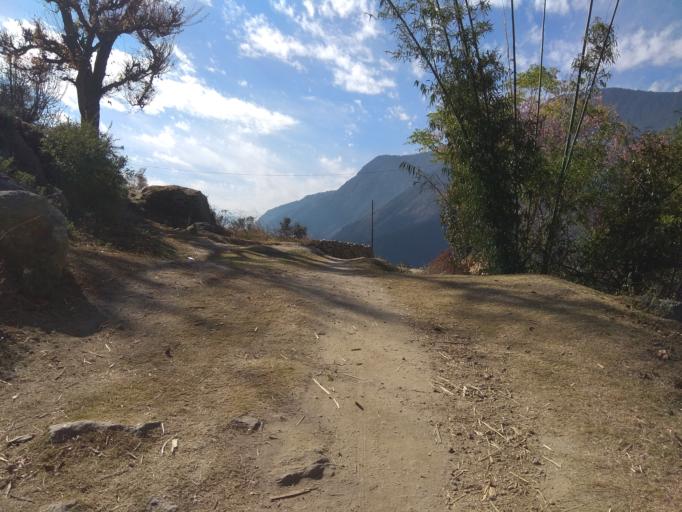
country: NP
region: Far Western
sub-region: Seti Zone
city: Achham
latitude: 29.2389
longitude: 81.6355
